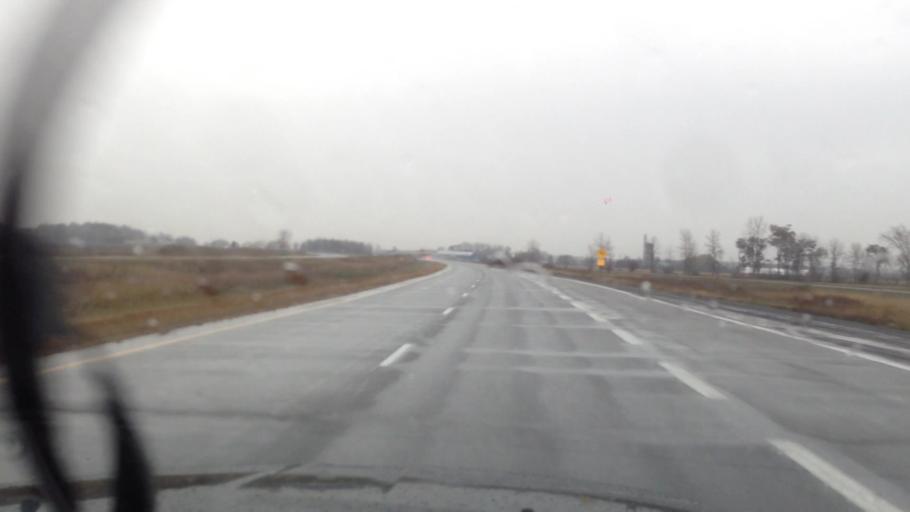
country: CA
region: Ontario
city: Casselman
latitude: 45.3443
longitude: -74.8974
